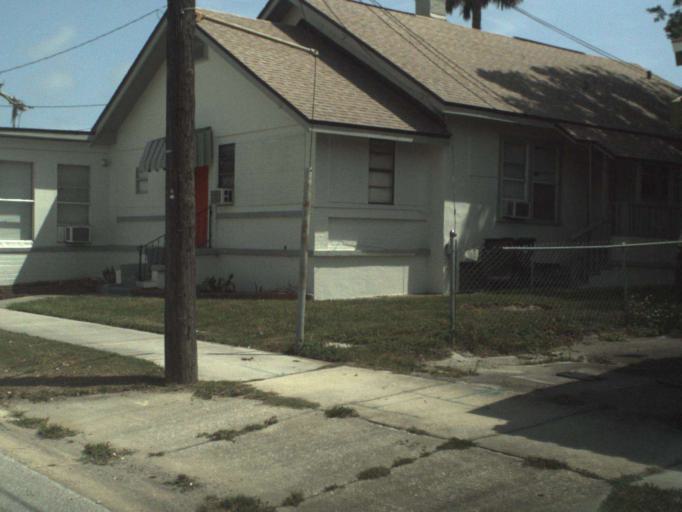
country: US
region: Florida
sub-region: Volusia County
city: Holly Hill
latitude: 29.2339
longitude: -81.0351
